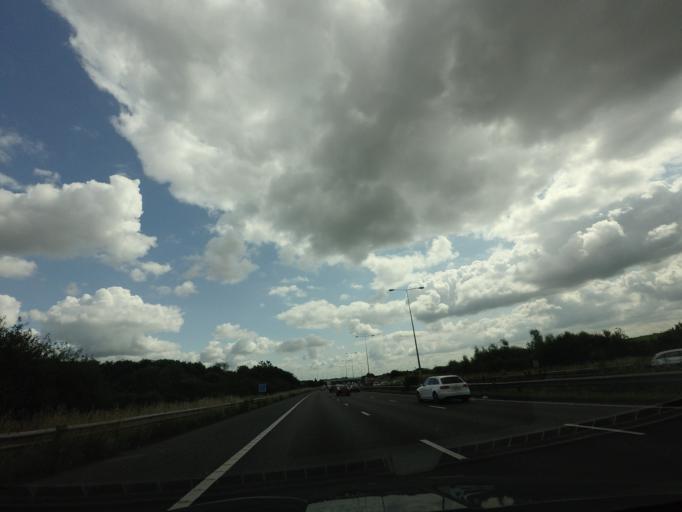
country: GB
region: England
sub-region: St. Helens
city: Billinge
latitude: 53.5103
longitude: -2.6744
